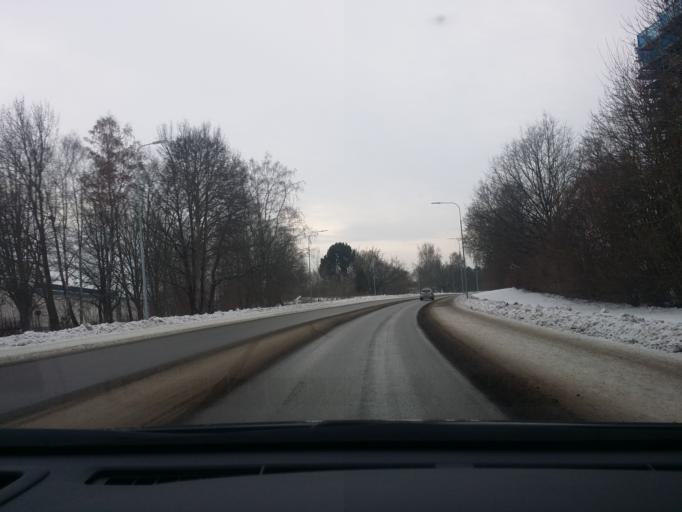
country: SE
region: Vaestra Goetaland
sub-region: Mariestads Kommun
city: Mariestad
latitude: 58.7006
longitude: 13.8199
